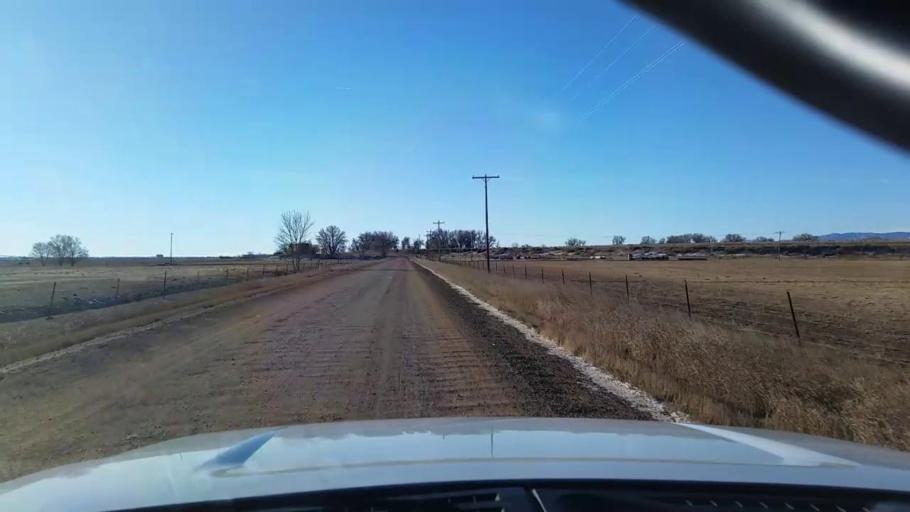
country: US
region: Colorado
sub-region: Larimer County
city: Wellington
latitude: 40.7641
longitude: -105.0380
